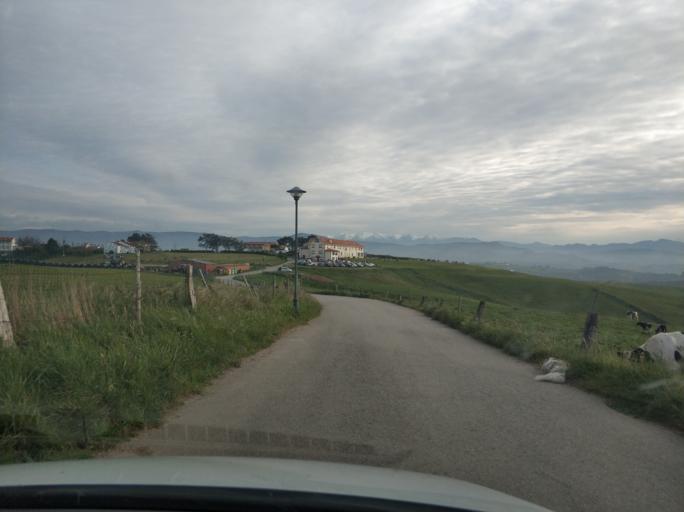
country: ES
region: Cantabria
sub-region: Provincia de Cantabria
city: San Vicente de la Barquera
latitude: 43.3983
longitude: -4.3504
